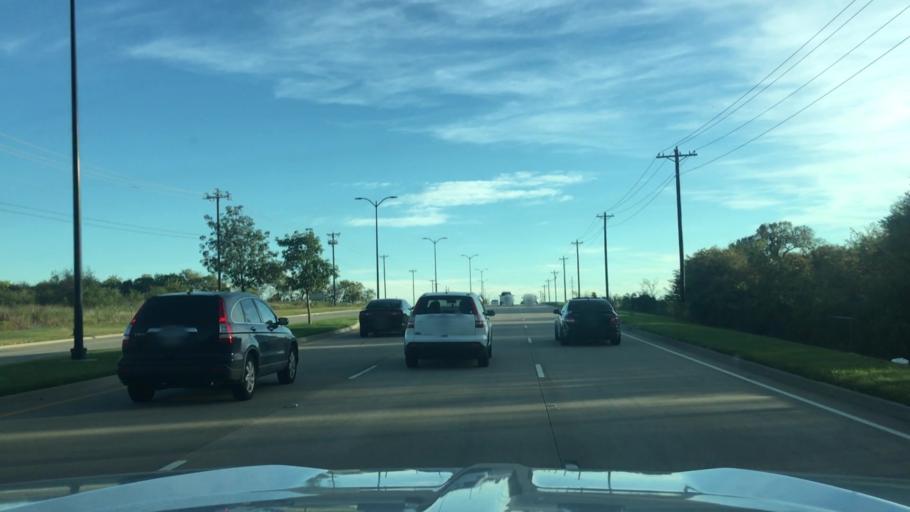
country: US
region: Texas
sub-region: Collin County
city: Prosper
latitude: 33.1956
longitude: -96.8030
